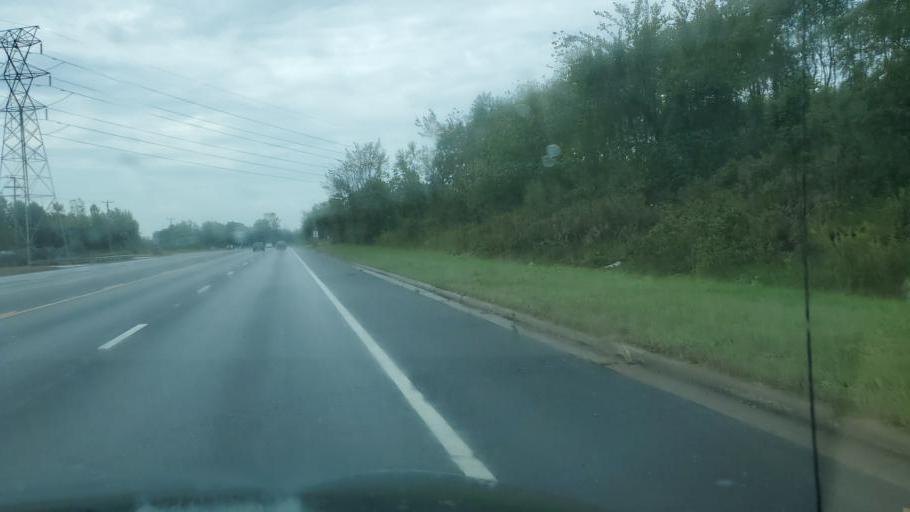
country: US
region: Ohio
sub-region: Licking County
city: Hebron
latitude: 39.9893
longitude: -82.4814
